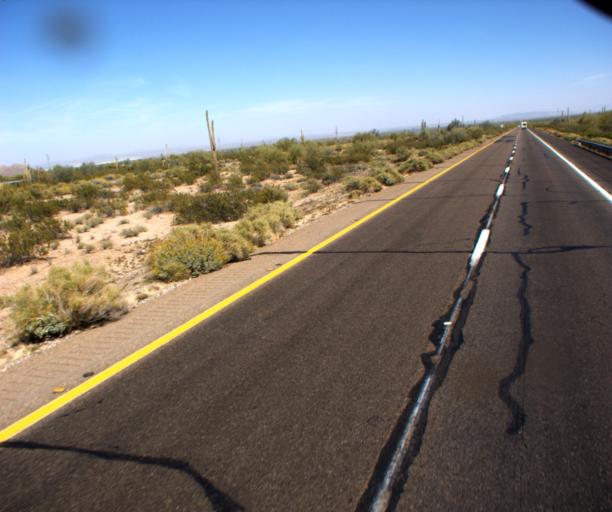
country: US
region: Arizona
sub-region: Pinal County
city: Maricopa
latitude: 32.8337
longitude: -112.1182
